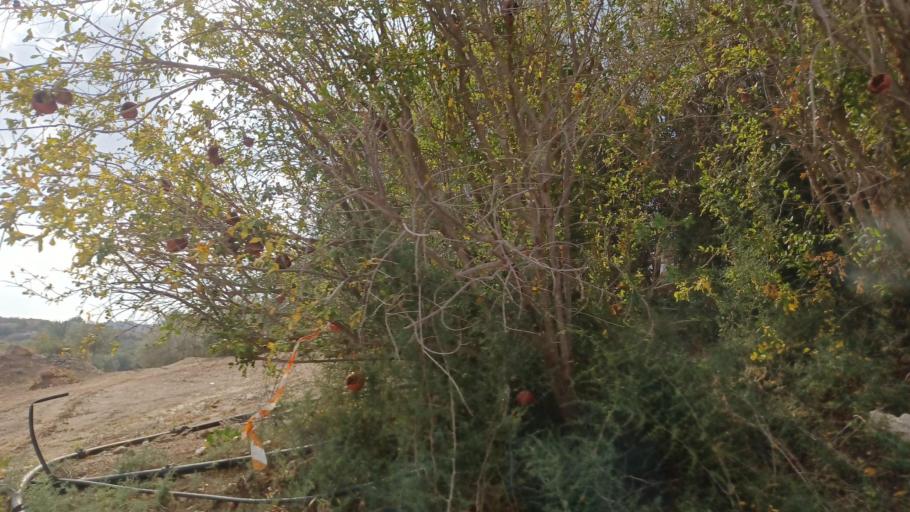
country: CY
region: Pafos
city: Kissonerga
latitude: 34.8437
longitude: 32.3947
